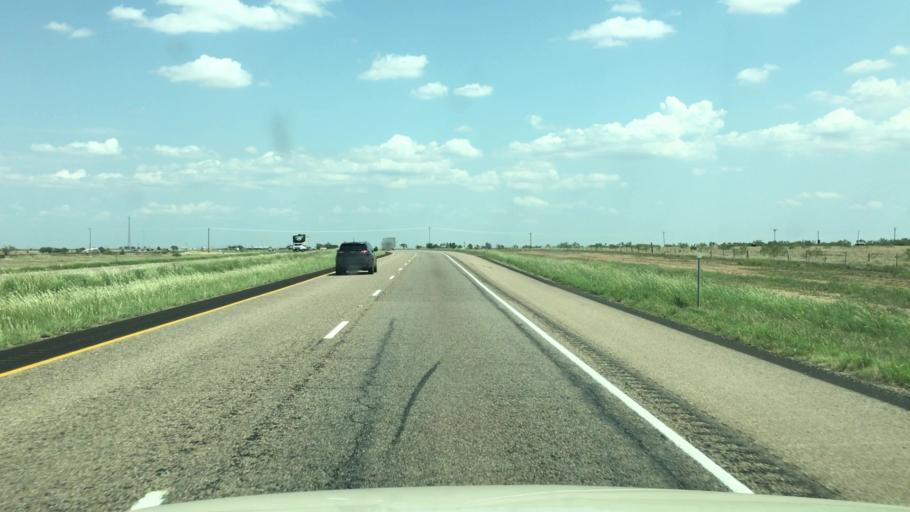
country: US
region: Texas
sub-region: Armstrong County
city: Claude
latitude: 35.0353
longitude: -101.1992
